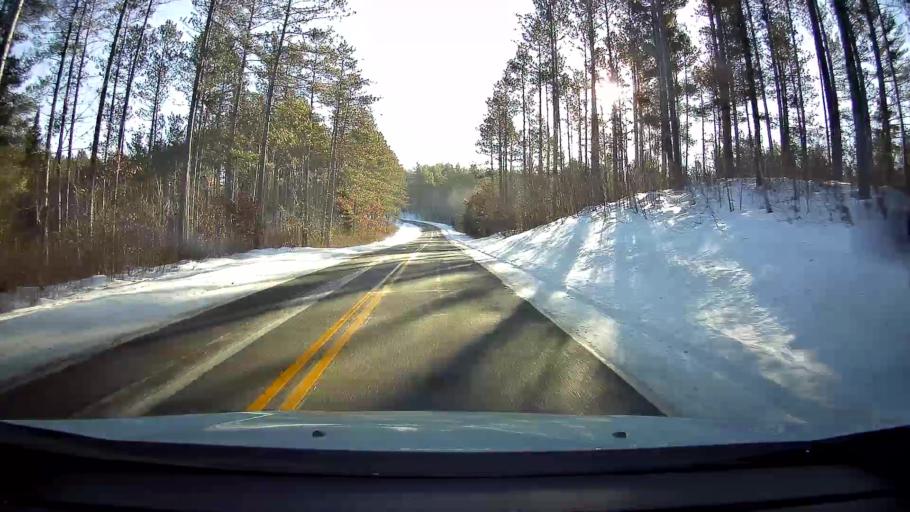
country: US
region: Wisconsin
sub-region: Sawyer County
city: Little Round Lake
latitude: 46.1102
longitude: -91.3044
